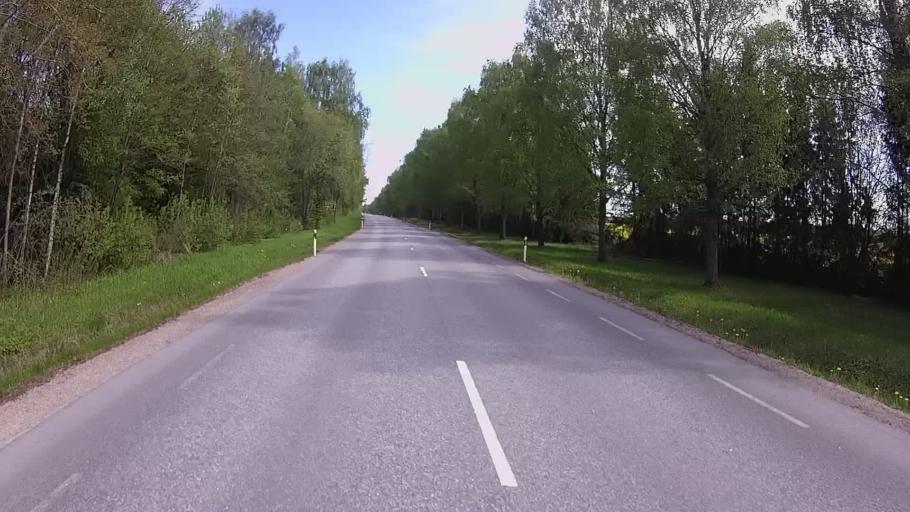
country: EE
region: Valgamaa
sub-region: Valga linn
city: Valga
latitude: 57.7316
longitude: 26.1567
